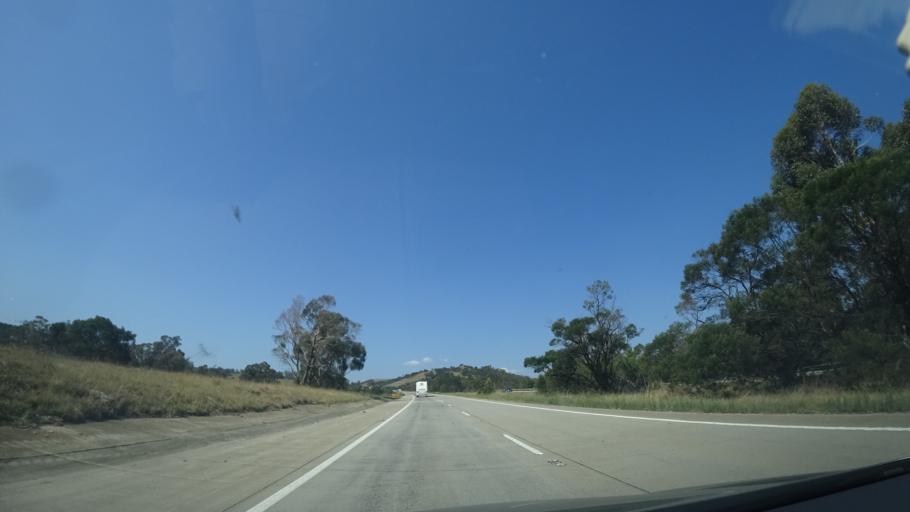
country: AU
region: New South Wales
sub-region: Wingecarribee
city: Bowral
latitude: -34.4645
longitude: 150.3502
